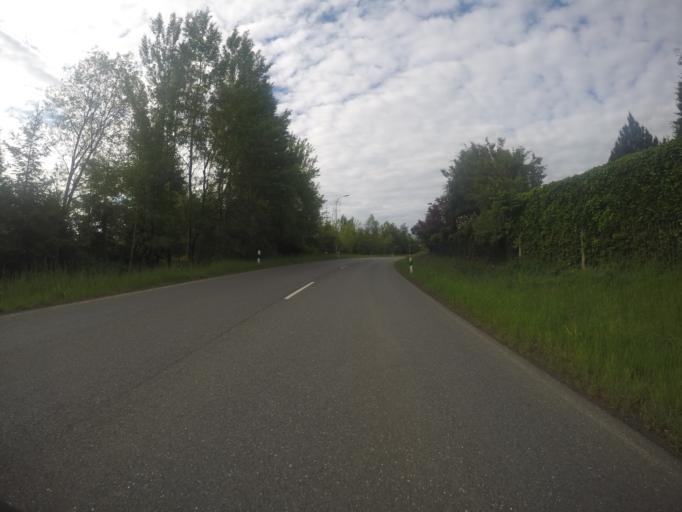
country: DE
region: Bavaria
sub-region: Upper Franconia
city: Schonwald
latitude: 50.2090
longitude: 12.0951
